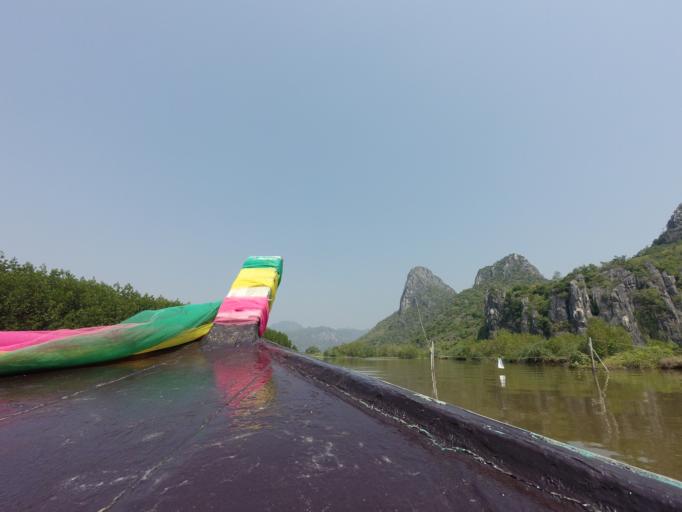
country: TH
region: Prachuap Khiri Khan
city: Kui Buri
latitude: 12.1427
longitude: 99.9525
